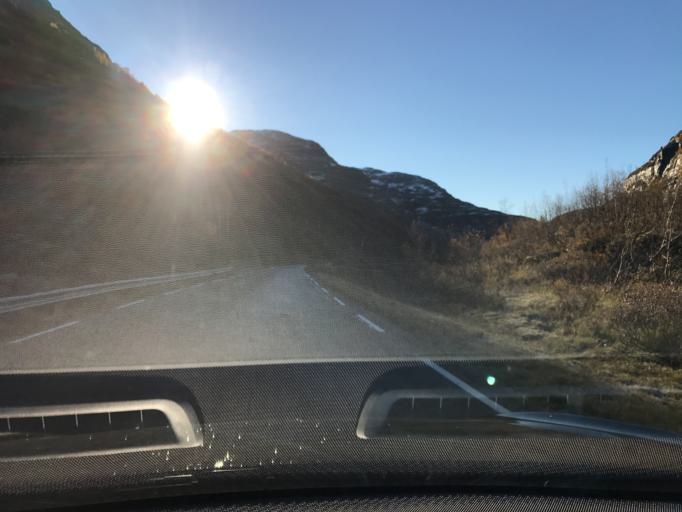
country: NO
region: Sogn og Fjordane
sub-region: Laerdal
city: Laerdalsoyri
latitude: 60.8128
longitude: 7.5549
